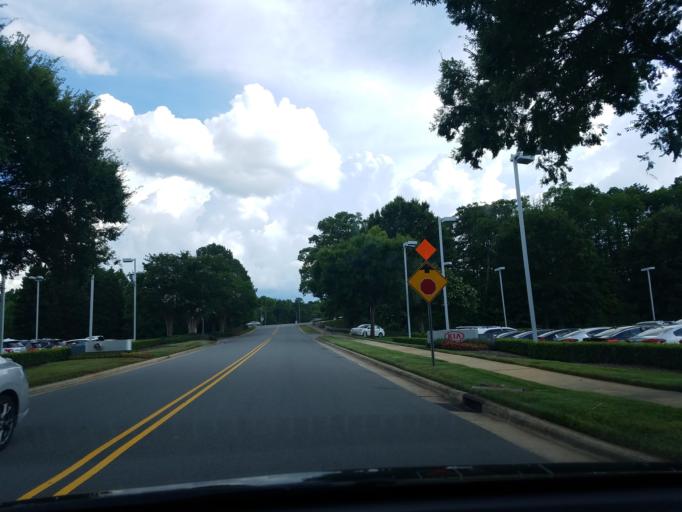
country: US
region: North Carolina
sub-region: Wake County
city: Apex
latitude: 35.7402
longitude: -78.8099
